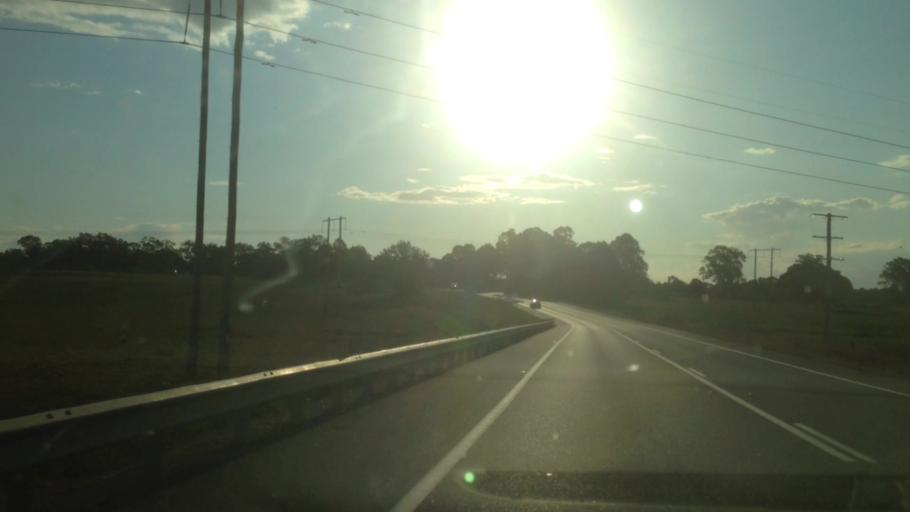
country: AU
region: New South Wales
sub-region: Cessnock
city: Heddon Greta
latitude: -32.8311
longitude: 151.5187
